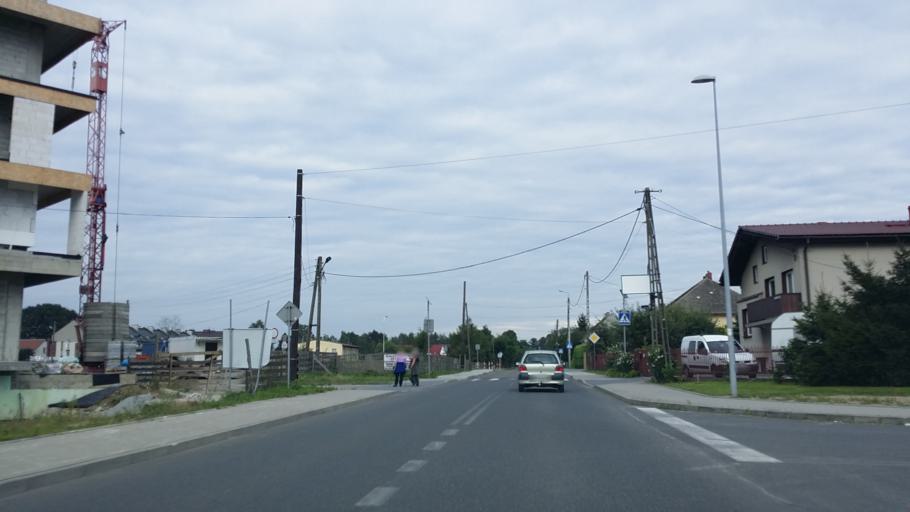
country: PL
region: Lesser Poland Voivodeship
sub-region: Powiat oswiecimski
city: Zator
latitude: 49.9928
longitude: 19.4310
